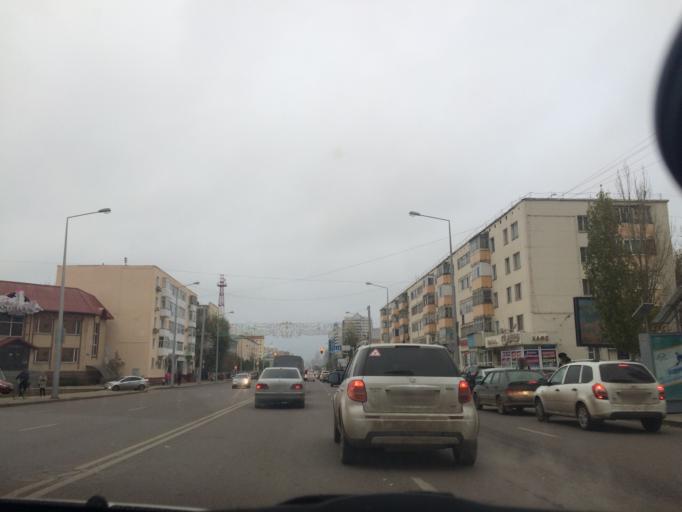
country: KZ
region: Astana Qalasy
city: Astana
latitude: 51.1738
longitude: 71.4067
